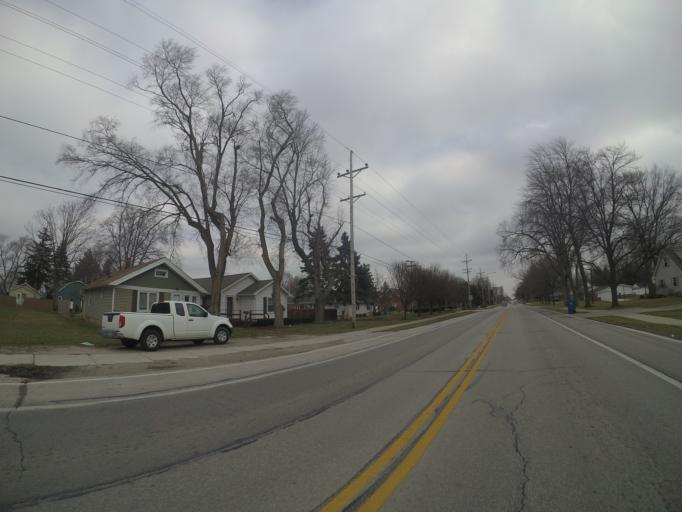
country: US
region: Ohio
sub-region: Lucas County
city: Oregon
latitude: 41.6440
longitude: -83.4831
